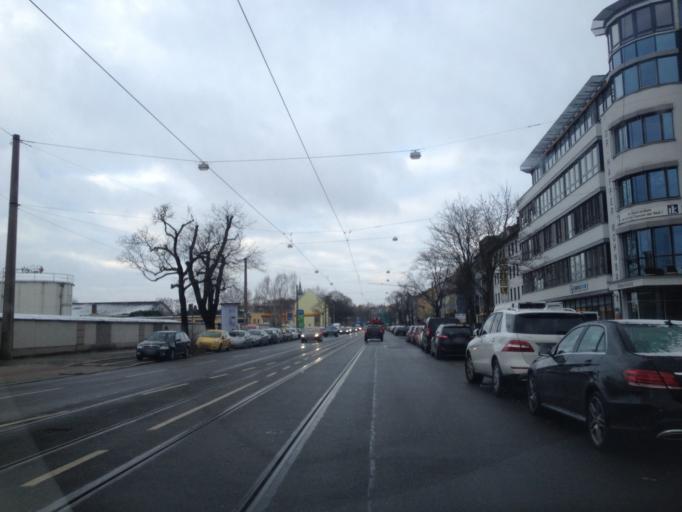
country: DE
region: Bavaria
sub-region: Regierungsbezirk Mittelfranken
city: Nuernberg
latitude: 49.4667
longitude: 11.1247
